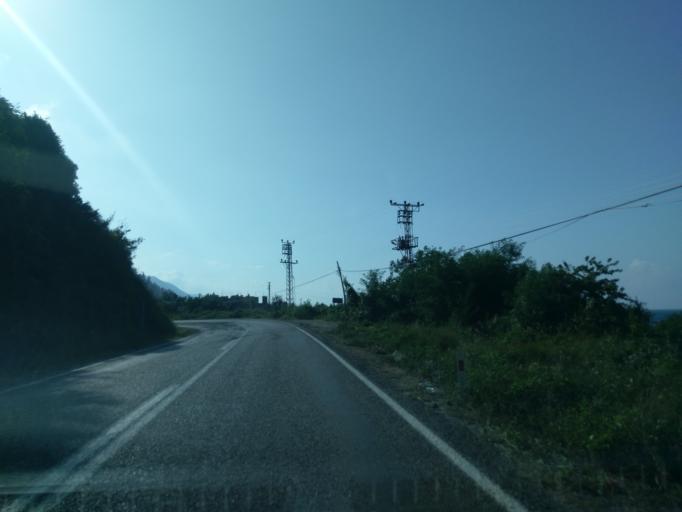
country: TR
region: Sinop
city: Ayancik
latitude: 41.9416
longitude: 34.6537
